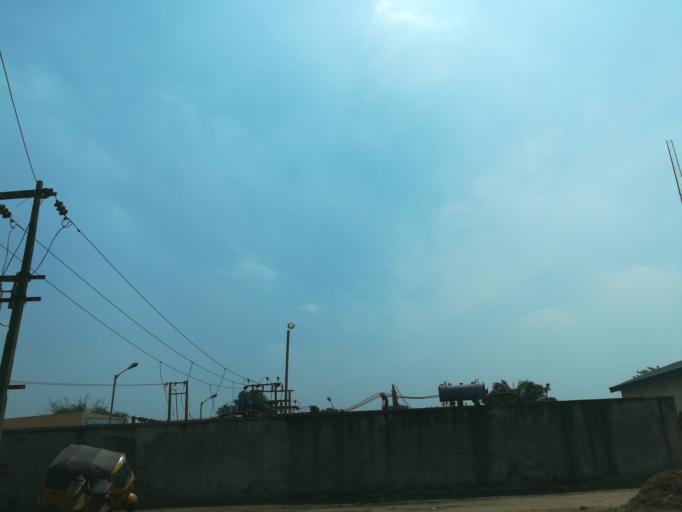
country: NG
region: Lagos
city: Ikorodu
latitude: 6.6412
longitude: 3.4807
